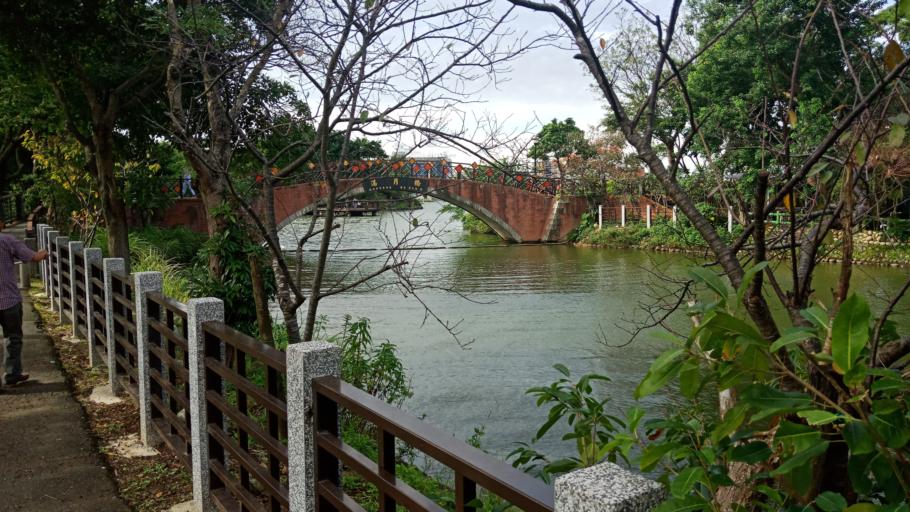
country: TW
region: Taiwan
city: Daxi
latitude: 24.8593
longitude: 121.2105
